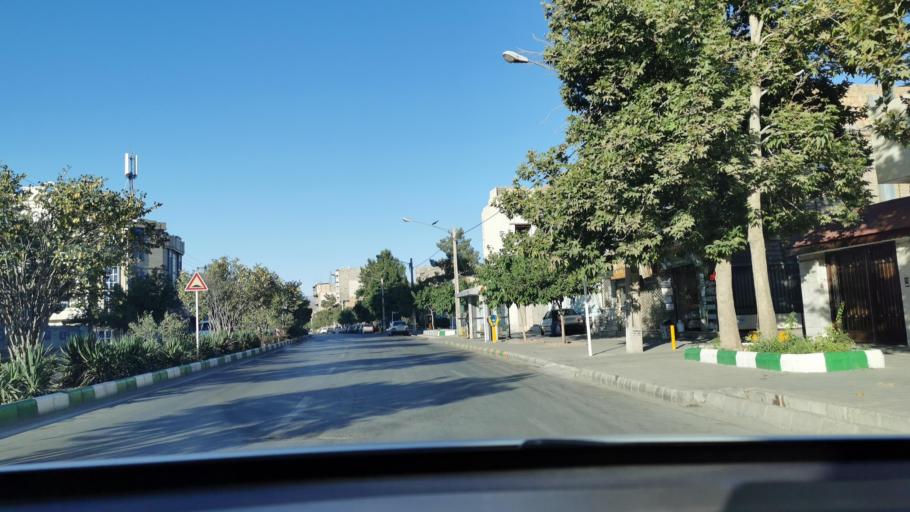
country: IR
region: Razavi Khorasan
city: Mashhad
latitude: 36.3498
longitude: 59.4788
